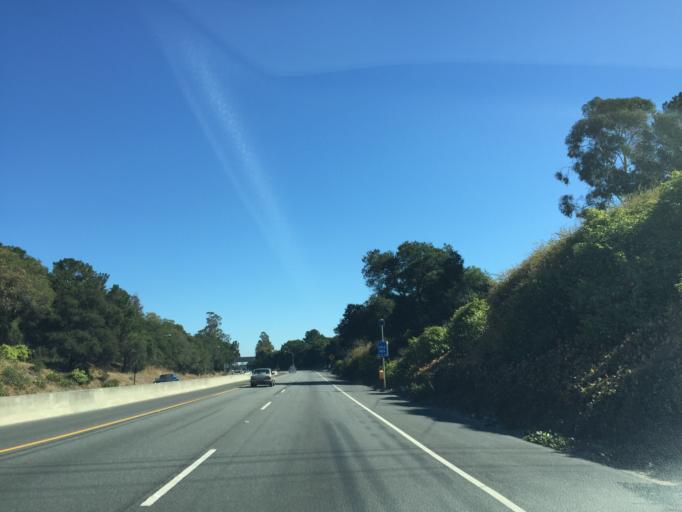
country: US
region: California
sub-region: San Mateo County
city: San Mateo
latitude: 37.5472
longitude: -122.3223
